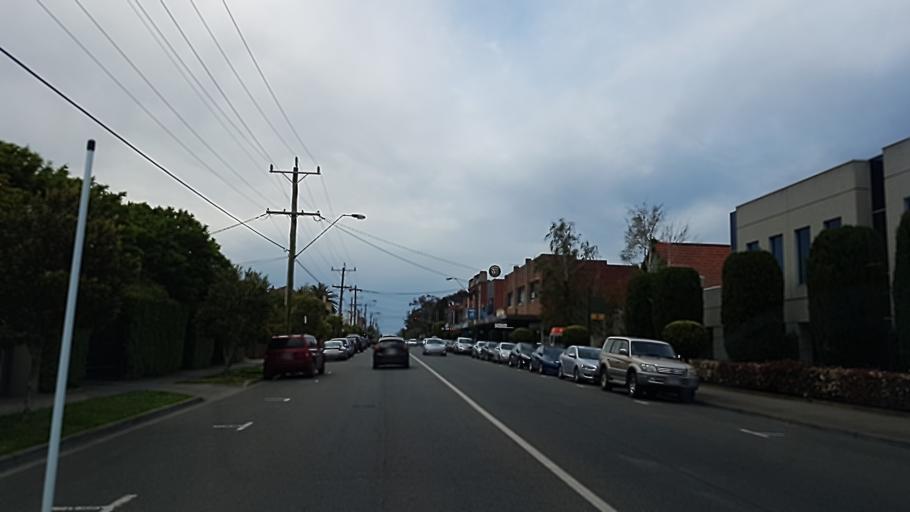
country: AU
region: Victoria
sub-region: Stonnington
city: Glen Iris
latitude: -37.8636
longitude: 145.0505
